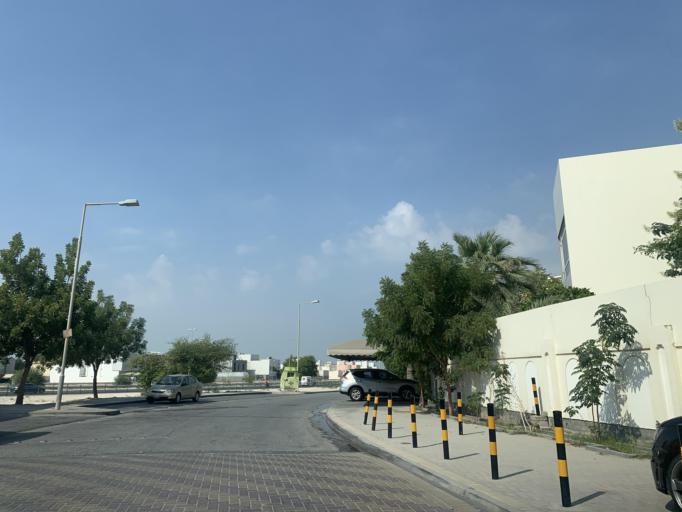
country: BH
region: Central Governorate
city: Madinat Hamad
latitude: 26.1062
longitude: 50.4983
